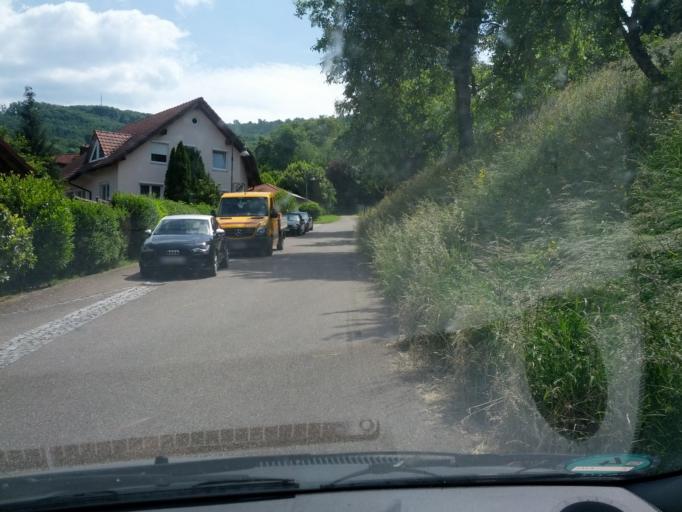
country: DE
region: Baden-Wuerttemberg
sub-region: Freiburg Region
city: Ebringen
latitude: 47.9561
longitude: 7.7828
